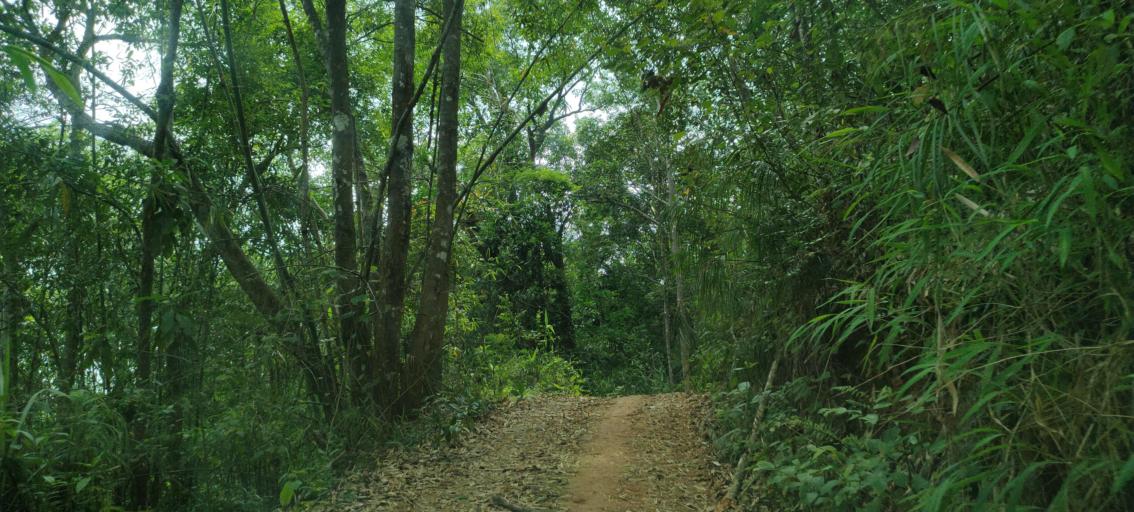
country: LA
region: Loungnamtha
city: Muang Nale
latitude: 20.4139
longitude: 101.4808
